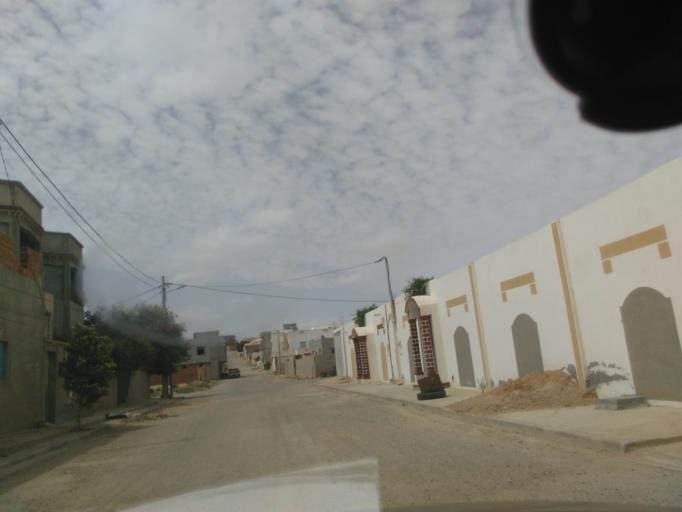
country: TN
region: Tataouine
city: Tataouine
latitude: 32.9482
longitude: 10.4711
